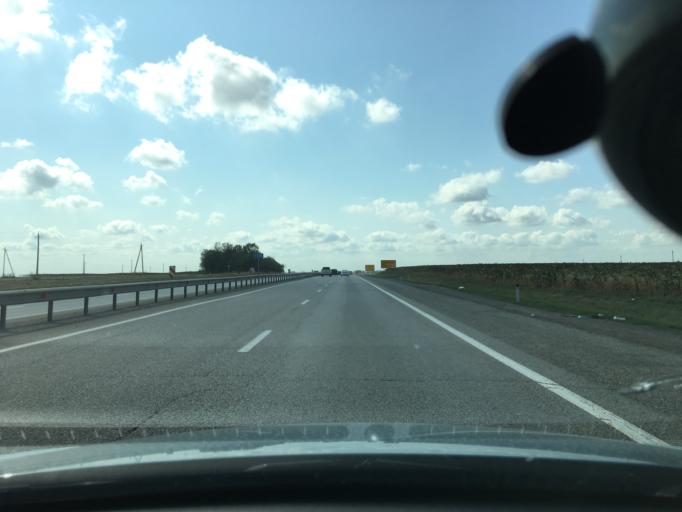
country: RU
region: Krasnodarskiy
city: Krasnoye
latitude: 46.7843
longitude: 39.6654
